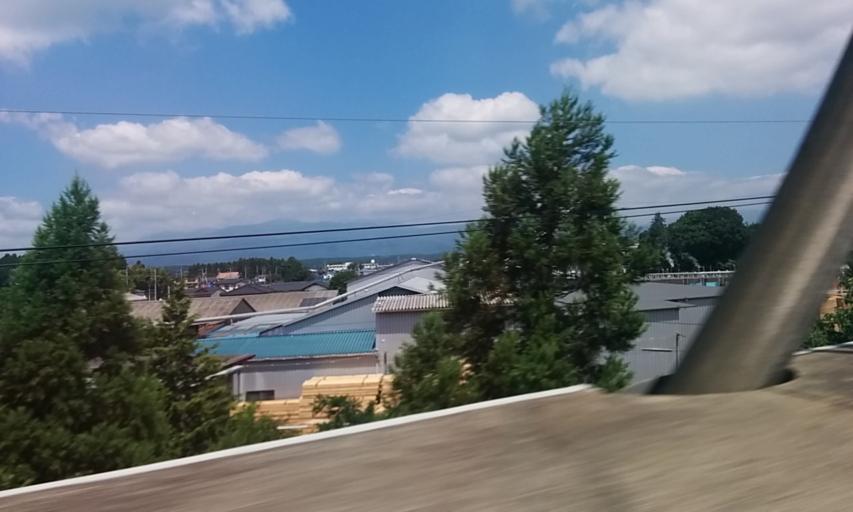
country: JP
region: Tochigi
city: Yaita
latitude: 36.8378
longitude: 139.9625
